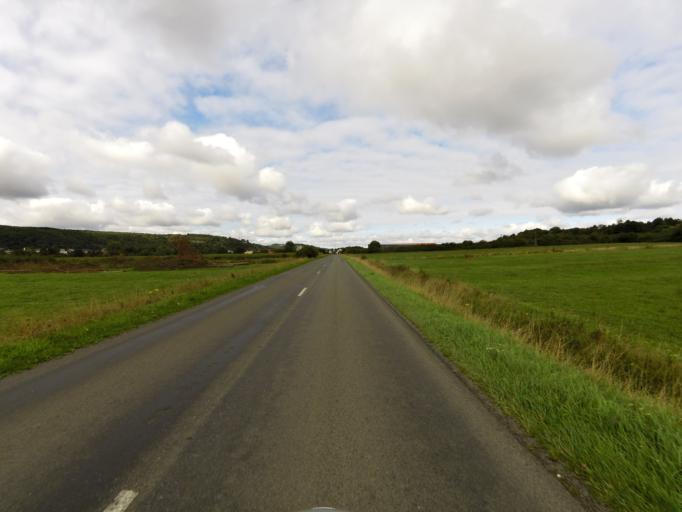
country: FR
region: Champagne-Ardenne
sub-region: Departement des Ardennes
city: Fromelennes
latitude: 50.1325
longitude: 4.8615
